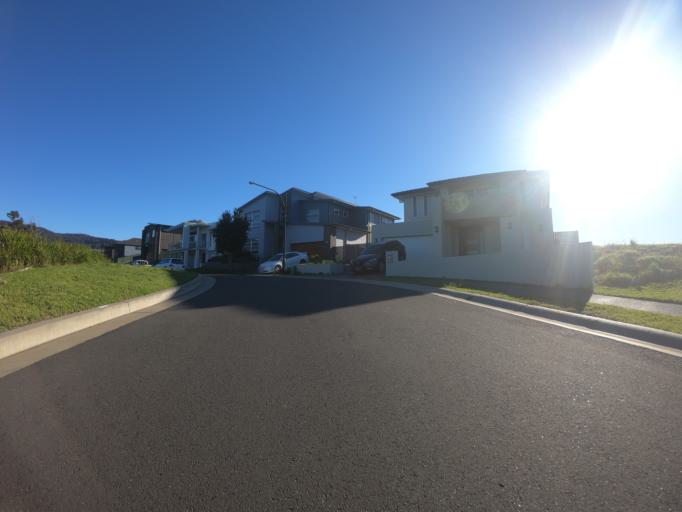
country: AU
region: New South Wales
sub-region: Wollongong
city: Cordeaux Heights
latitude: -34.4404
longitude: 150.8430
